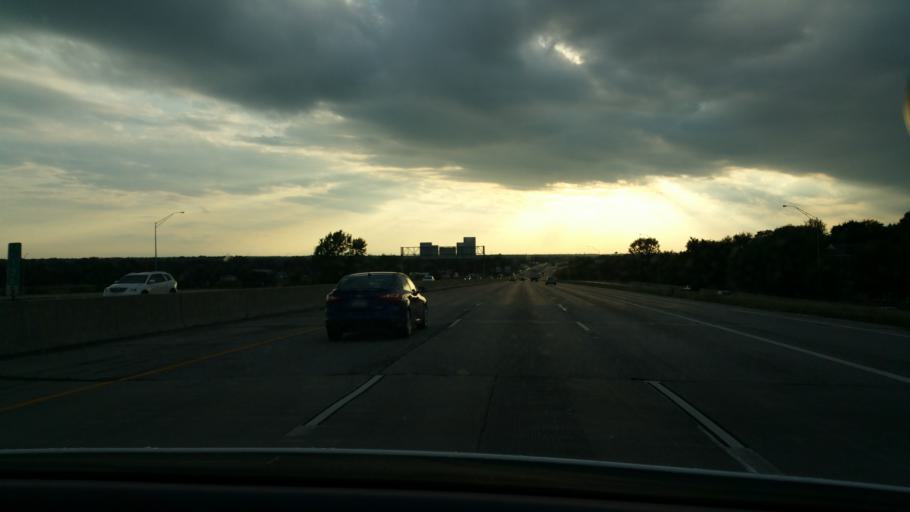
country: US
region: Iowa
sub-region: Polk County
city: Saylorville
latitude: 41.6500
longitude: -93.6008
